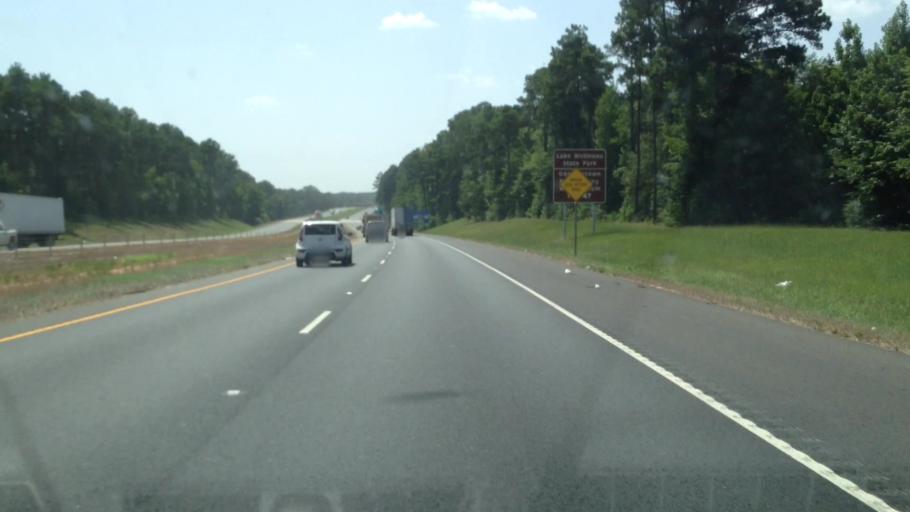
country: US
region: Louisiana
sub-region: Webster Parish
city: Minden
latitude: 32.5874
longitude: -93.2801
